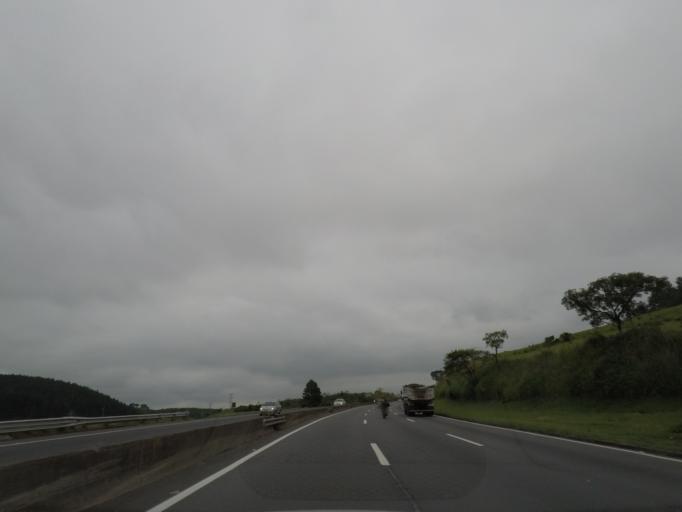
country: BR
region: Sao Paulo
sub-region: Aparecida
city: Aparecida
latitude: -22.8672
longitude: -45.2425
